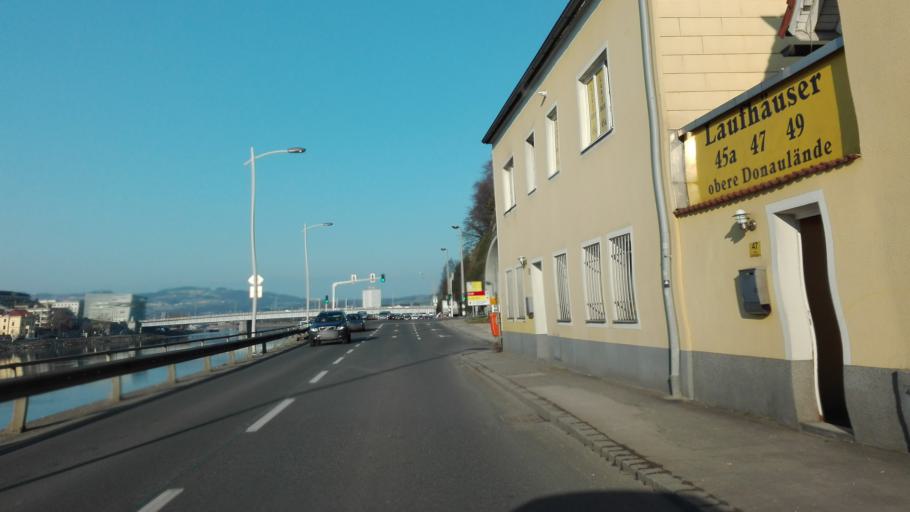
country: AT
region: Upper Austria
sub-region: Linz Stadt
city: Linz
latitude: 48.3052
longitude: 14.2782
